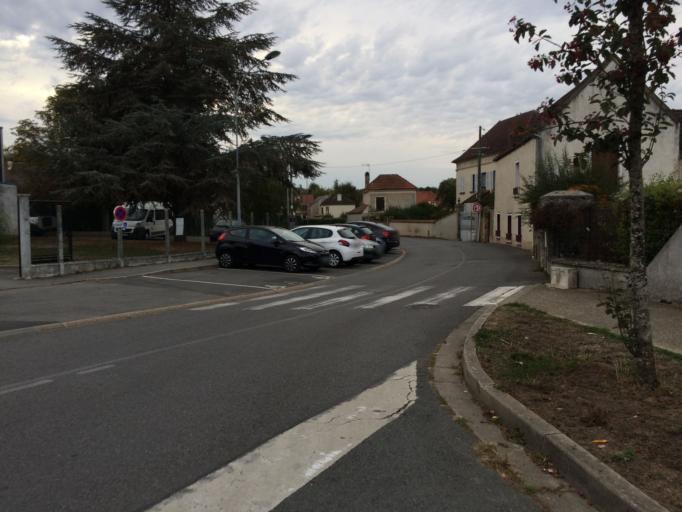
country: FR
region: Ile-de-France
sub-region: Departement de l'Essonne
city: Marcoussis
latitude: 48.6403
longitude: 2.2311
